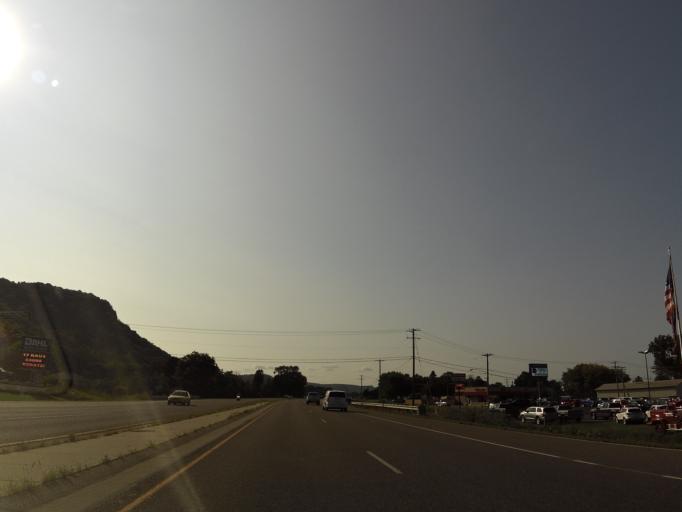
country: US
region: Minnesota
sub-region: Winona County
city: Winona
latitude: 44.0448
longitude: -91.6692
